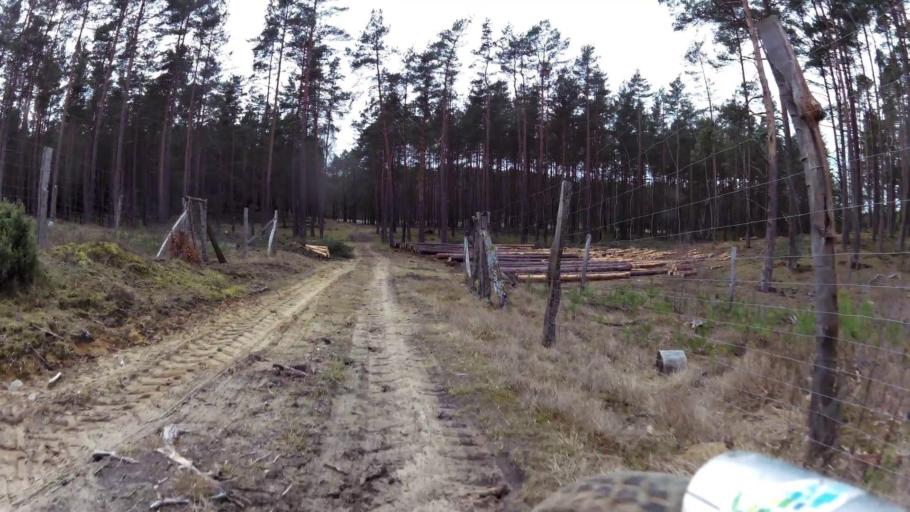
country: PL
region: Pomeranian Voivodeship
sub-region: Powiat bytowski
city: Trzebielino
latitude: 54.1504
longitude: 17.1620
